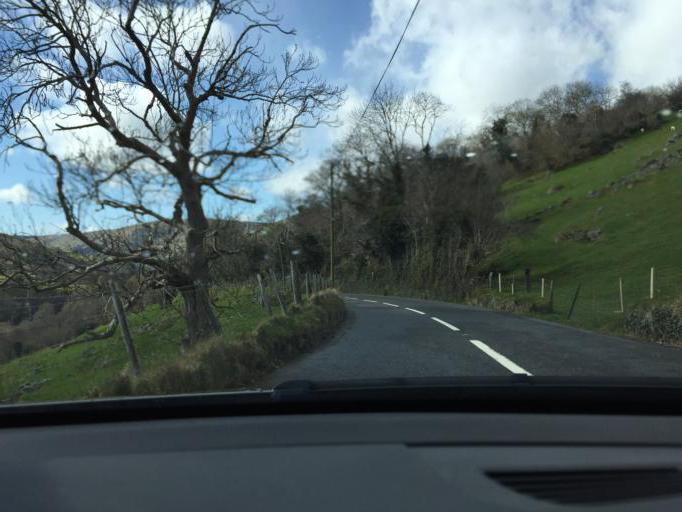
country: GB
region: Northern Ireland
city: Cushendall
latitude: 55.1240
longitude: -6.0880
